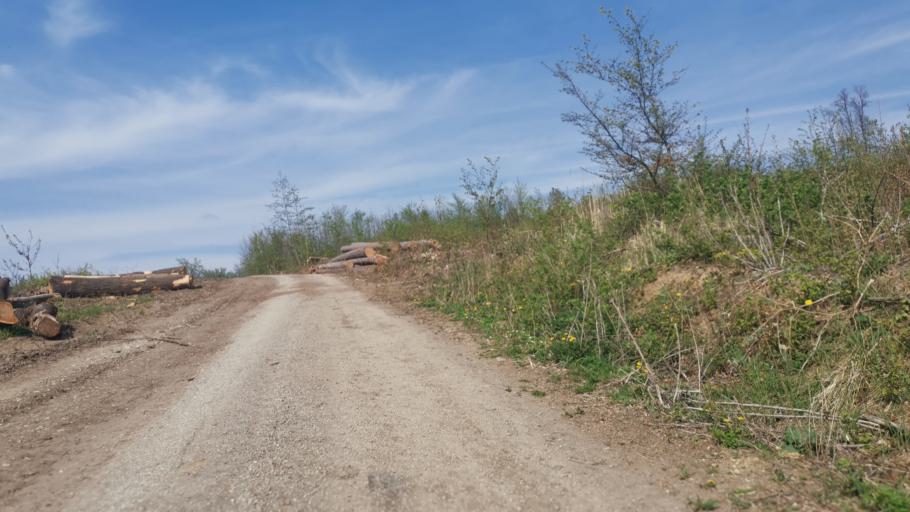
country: SK
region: Trnavsky
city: Smolenice
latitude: 48.5647
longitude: 17.3573
